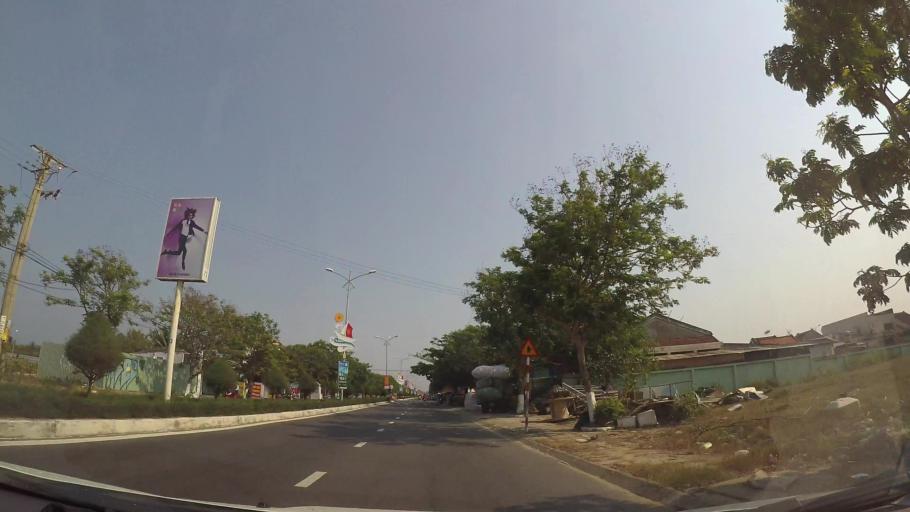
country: VN
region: Da Nang
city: Ngu Hanh Son
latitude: 15.9581
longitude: 108.2912
